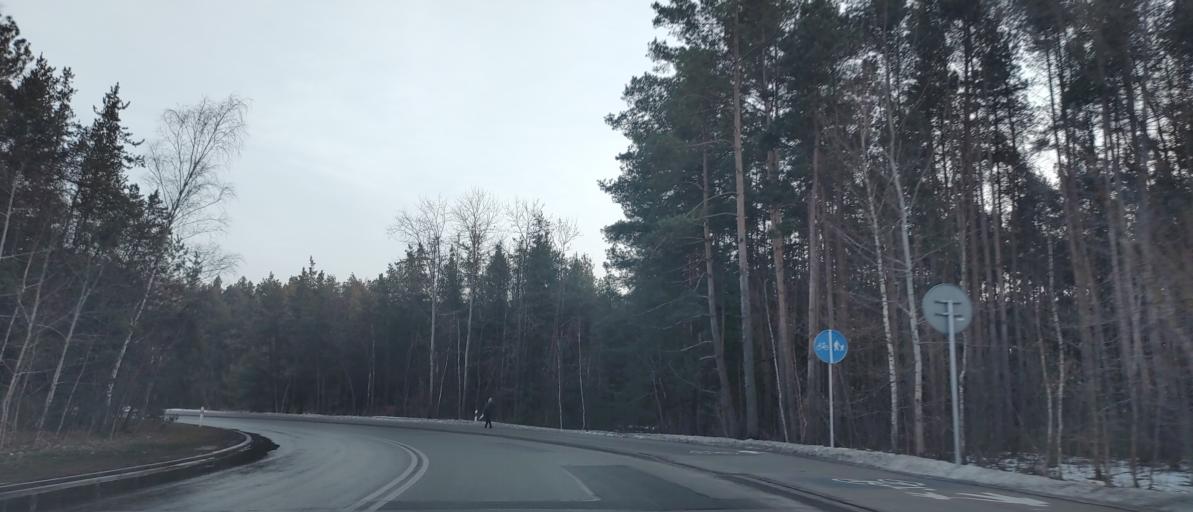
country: PL
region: Masovian Voivodeship
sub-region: Powiat bialobrzeski
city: Bialobrzegi
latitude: 51.6442
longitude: 20.9330
